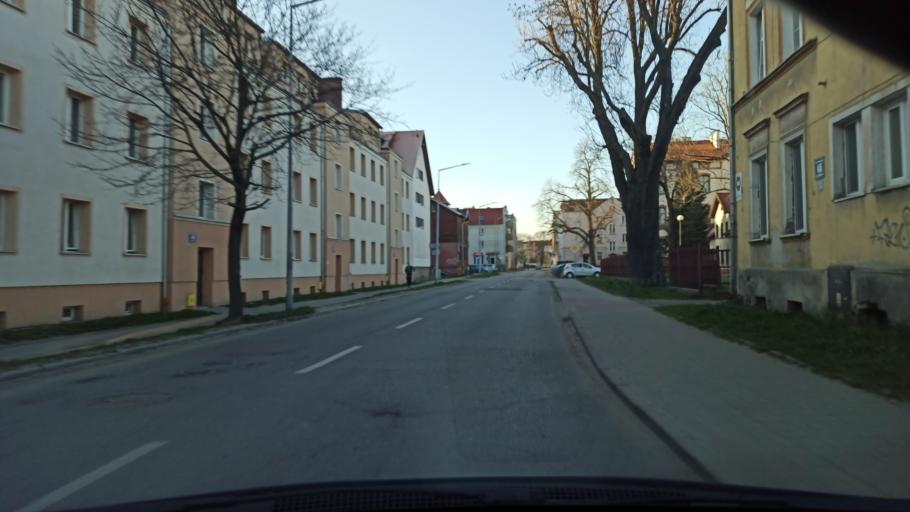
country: PL
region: Warmian-Masurian Voivodeship
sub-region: Powiat elblaski
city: Elblag
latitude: 54.1534
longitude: 19.4020
